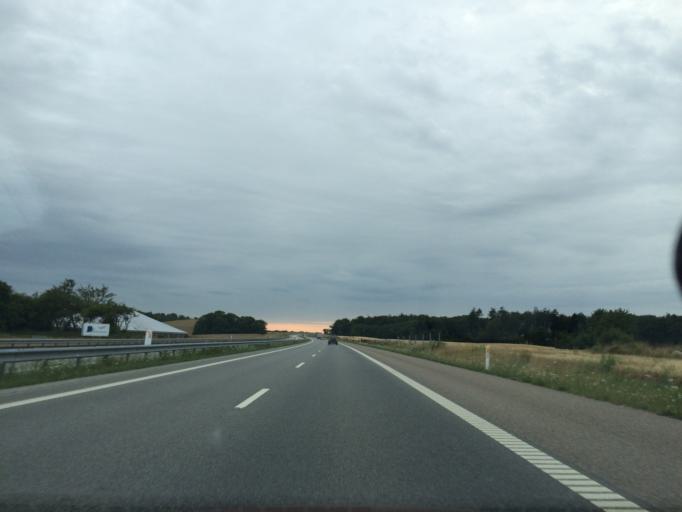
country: DK
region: South Denmark
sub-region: Sonderborg Kommune
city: Grasten
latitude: 54.9594
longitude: 9.5963
